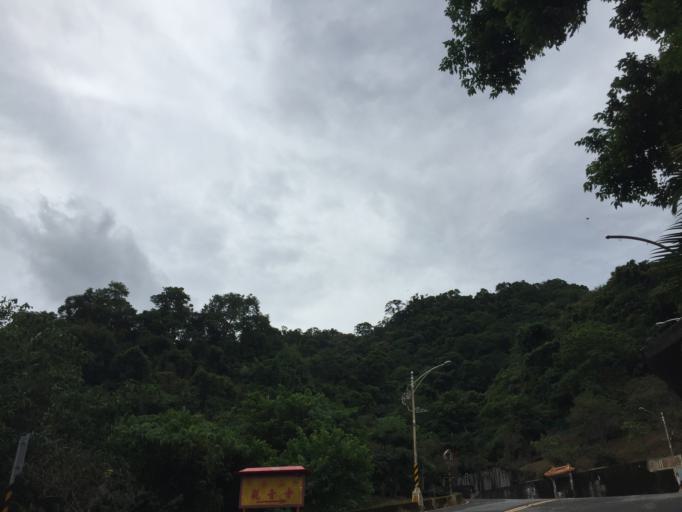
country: TW
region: Taipei
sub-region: Taipei
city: Banqiao
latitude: 24.9736
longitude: 121.5008
